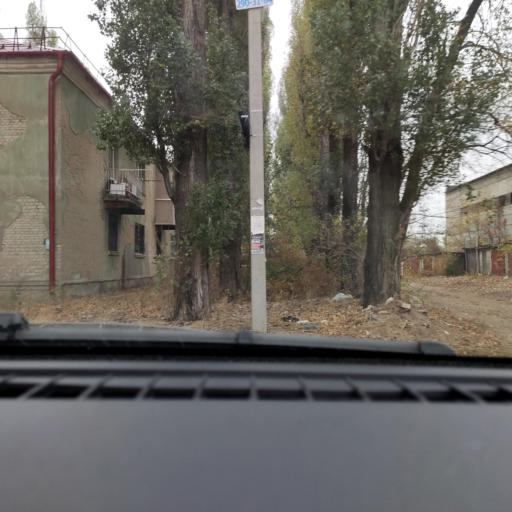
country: RU
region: Voronezj
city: Voronezh
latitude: 51.6357
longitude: 39.2608
